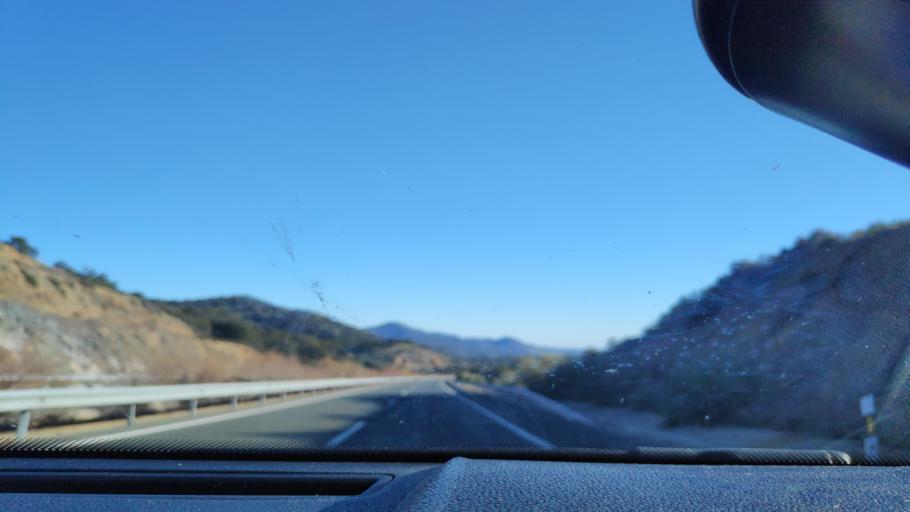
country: ES
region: Extremadura
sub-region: Provincia de Badajoz
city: Monesterio
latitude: 38.0715
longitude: -6.2504
